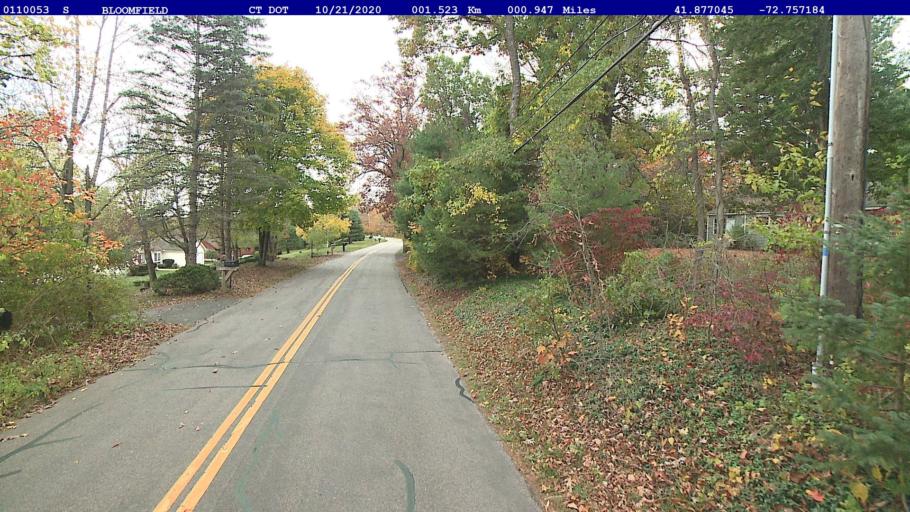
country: US
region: Connecticut
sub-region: Hartford County
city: Tariffville
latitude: 41.8770
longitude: -72.7572
